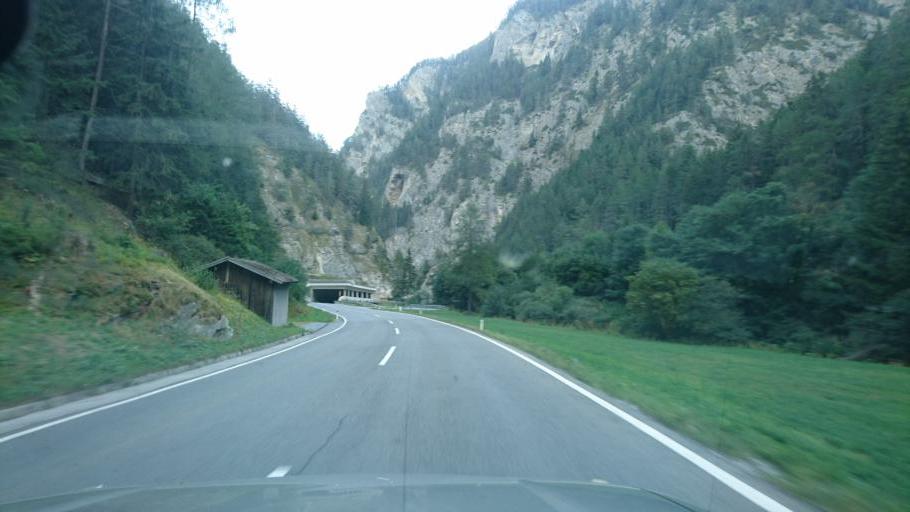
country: AT
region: Tyrol
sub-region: Politischer Bezirk Landeck
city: Nauders
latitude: 46.9087
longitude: 10.4963
